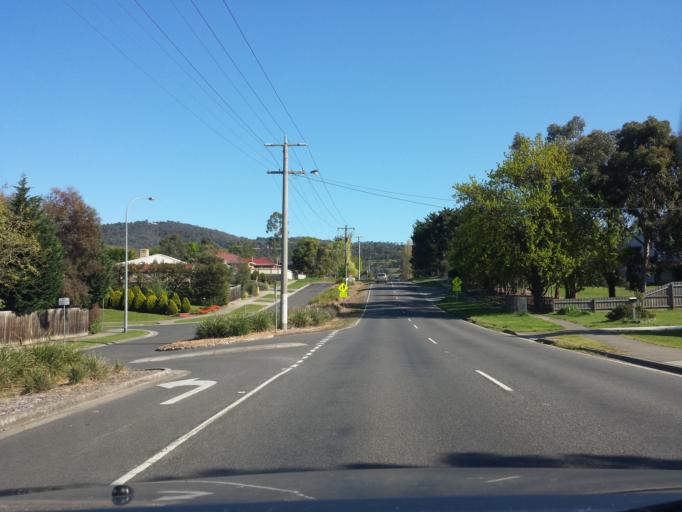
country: AU
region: Victoria
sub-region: Yarra Ranges
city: Yarra Glen
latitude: -37.6506
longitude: 145.3734
